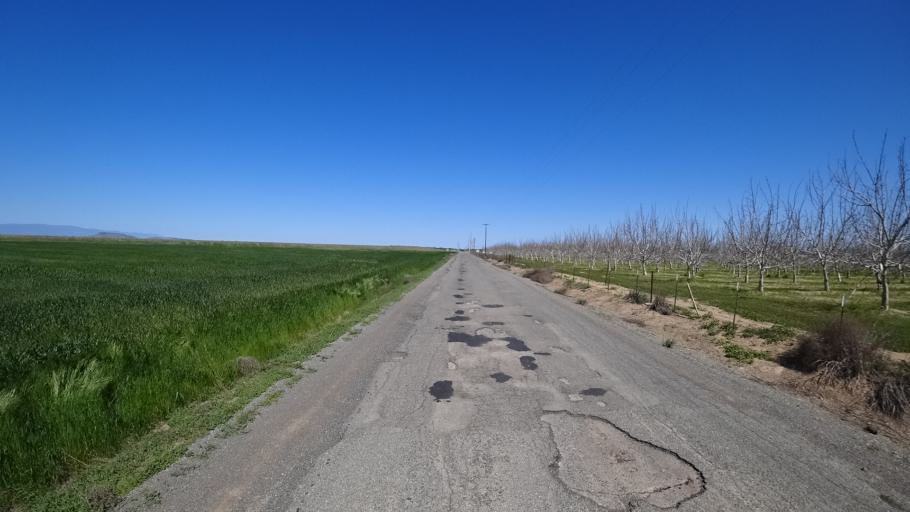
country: US
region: California
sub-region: Glenn County
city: Orland
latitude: 39.6865
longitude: -122.2342
